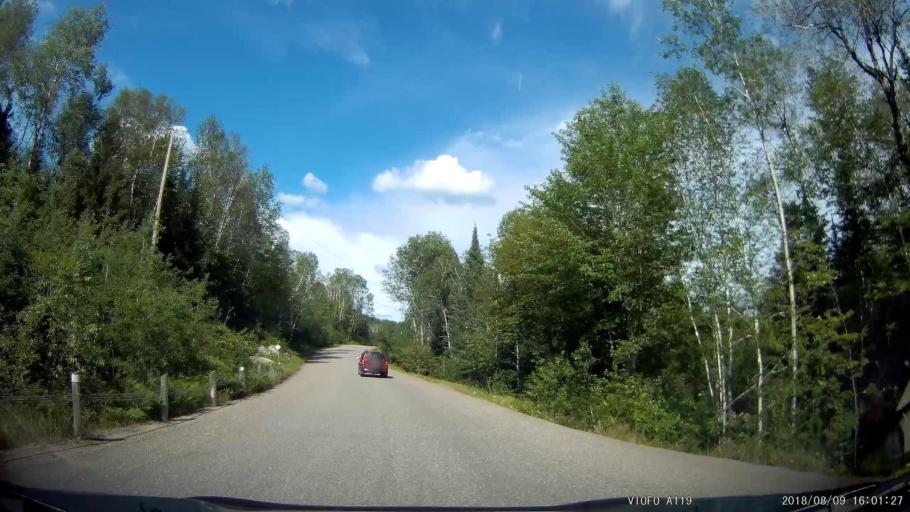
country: CA
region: Ontario
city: Rayside-Balfour
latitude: 46.6133
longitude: -81.4698
